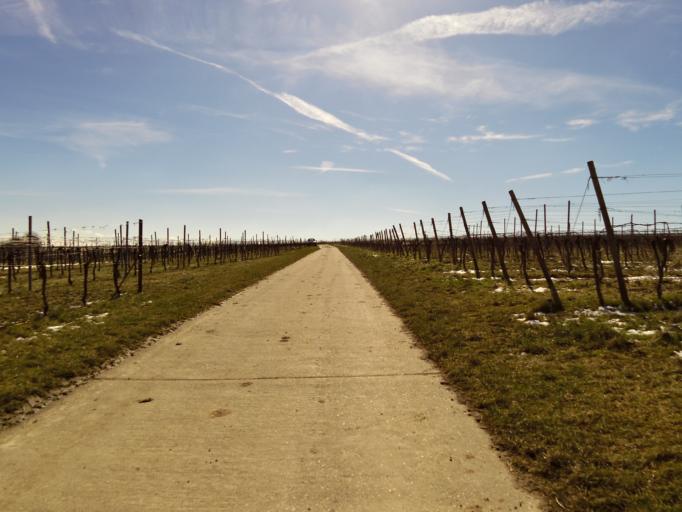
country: DE
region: Rheinland-Pfalz
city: Kindenheim
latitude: 49.6058
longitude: 8.1660
